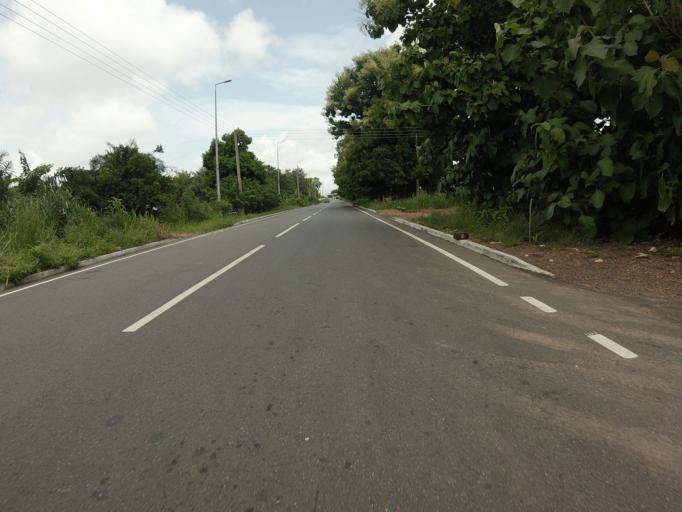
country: GH
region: Volta
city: Ho
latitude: 6.6062
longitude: 0.4604
